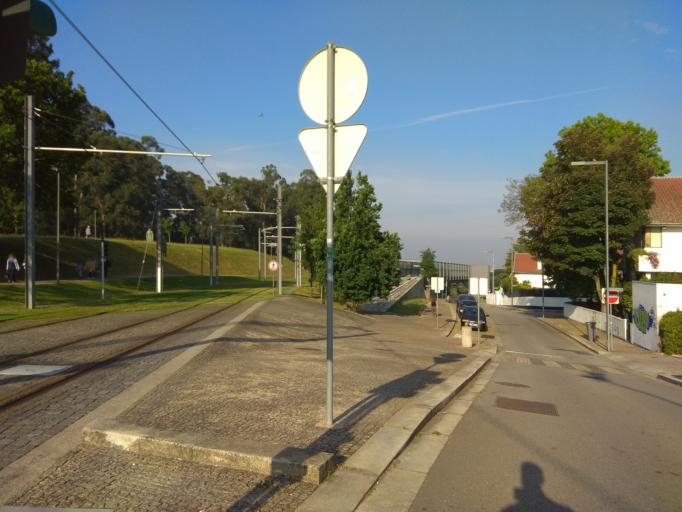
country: PT
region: Porto
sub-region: Maia
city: Maia
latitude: 41.2296
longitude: -8.6241
